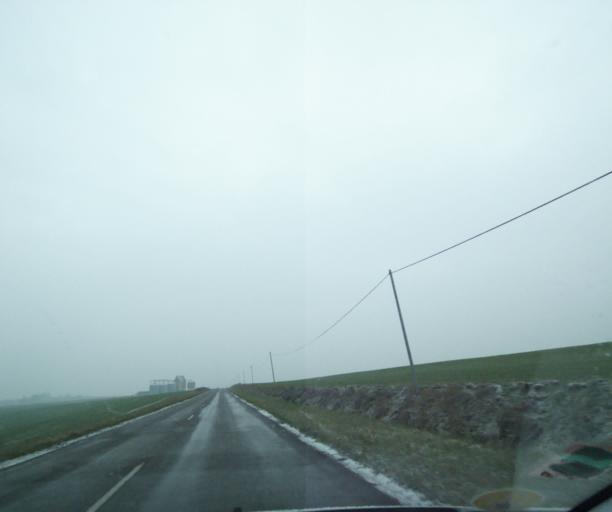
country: FR
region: Champagne-Ardenne
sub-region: Departement de la Haute-Marne
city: Wassy
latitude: 48.4870
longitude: 4.9794
